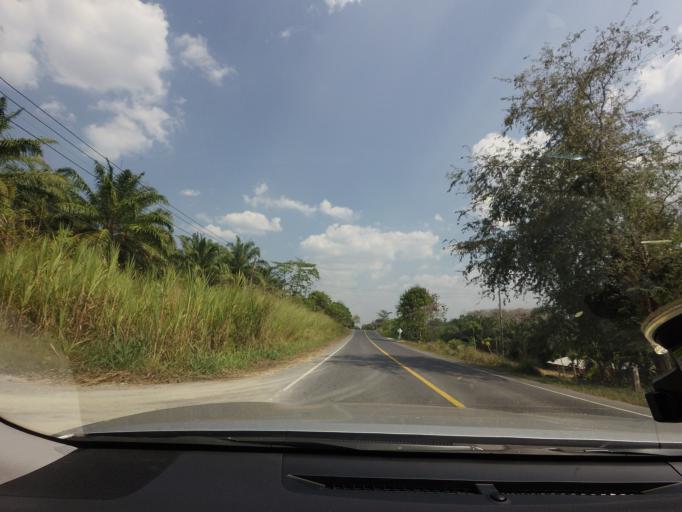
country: TH
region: Phangnga
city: Thap Put
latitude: 8.5329
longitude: 98.6241
